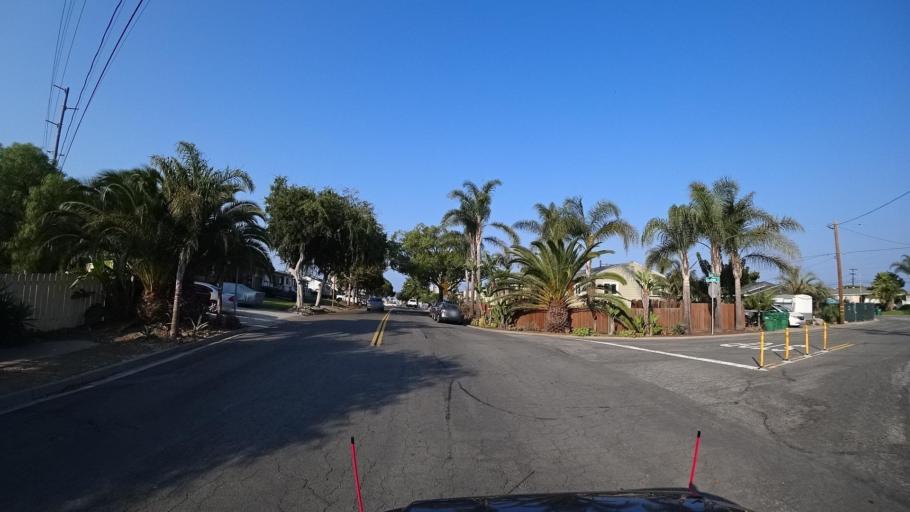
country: US
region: California
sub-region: San Diego County
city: Oceanside
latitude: 33.2113
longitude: -117.3831
